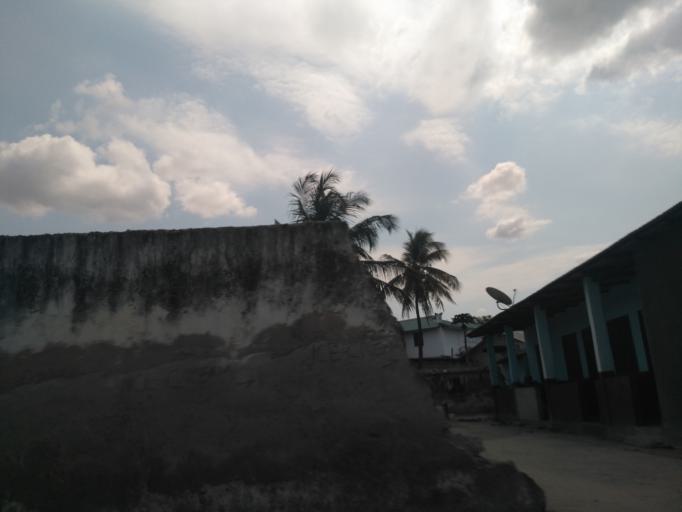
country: TZ
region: Dar es Salaam
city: Dar es Salaam
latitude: -6.8250
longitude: 39.3074
